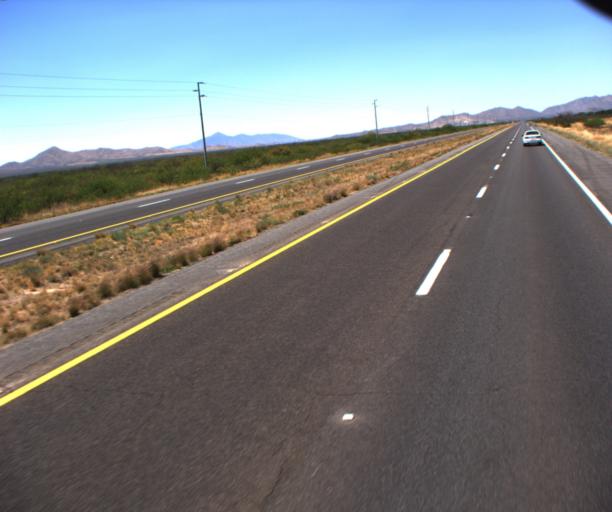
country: US
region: Arizona
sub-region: Cochise County
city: Pirtleville
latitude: 31.3613
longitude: -109.6686
